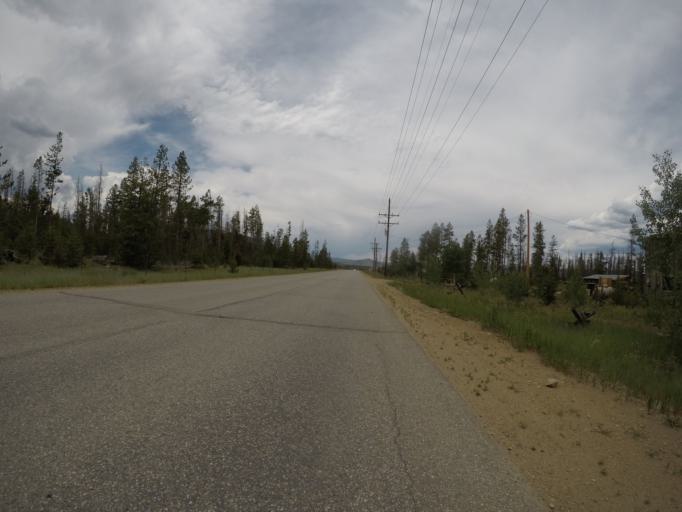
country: US
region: Colorado
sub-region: Grand County
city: Fraser
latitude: 39.9572
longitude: -105.8456
